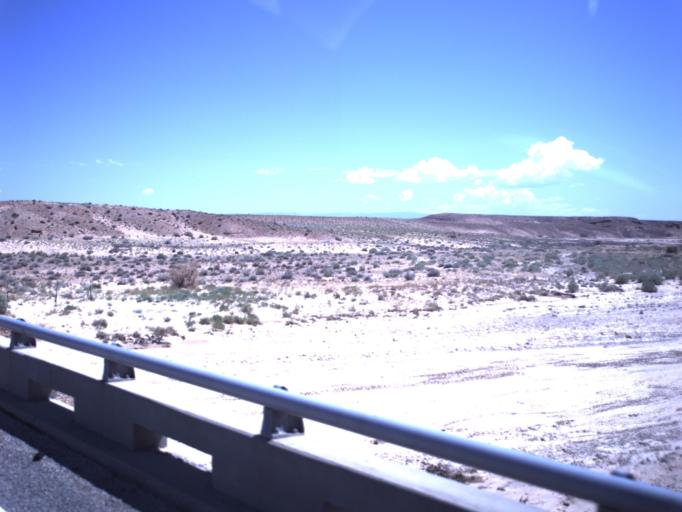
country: US
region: Utah
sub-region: Emery County
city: Castle Dale
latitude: 38.7747
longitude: -110.4408
